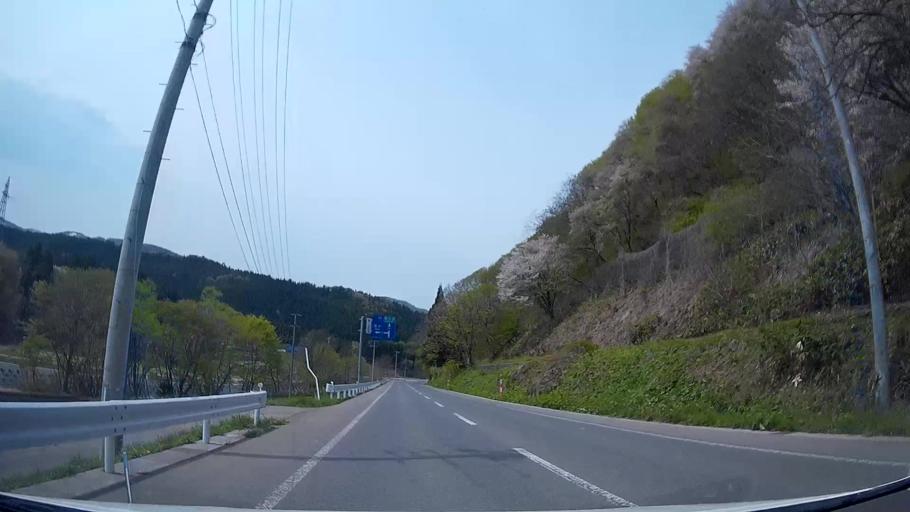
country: JP
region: Akita
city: Hanawa
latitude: 40.0760
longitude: 140.7951
